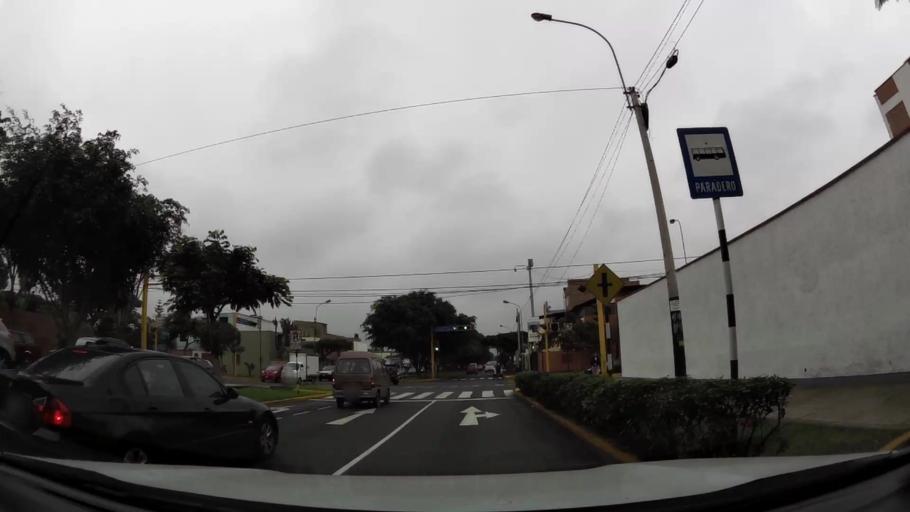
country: PE
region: Lima
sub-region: Lima
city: Surco
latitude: -12.1374
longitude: -77.0035
